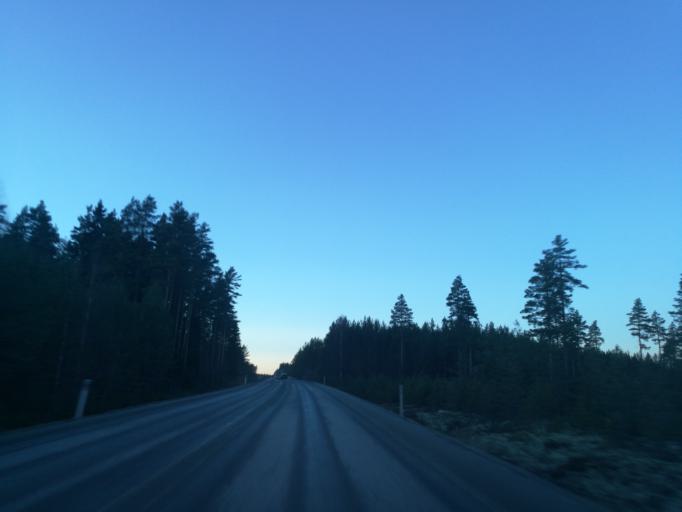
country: NO
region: Hedmark
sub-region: Eidskog
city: Skotterud
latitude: 59.9393
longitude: 12.1904
